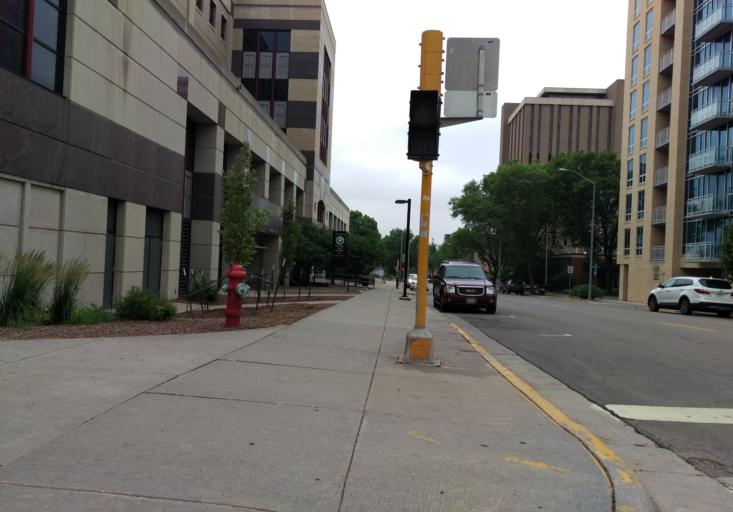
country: US
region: Wisconsin
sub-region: Dane County
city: Madison
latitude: 43.0732
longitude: -89.4023
